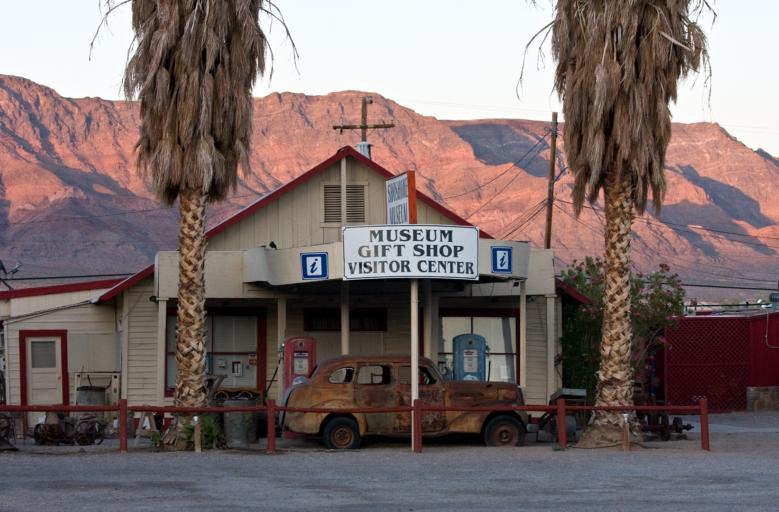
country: US
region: Nevada
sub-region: Nye County
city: Pahrump
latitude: 35.9749
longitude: -116.2706
